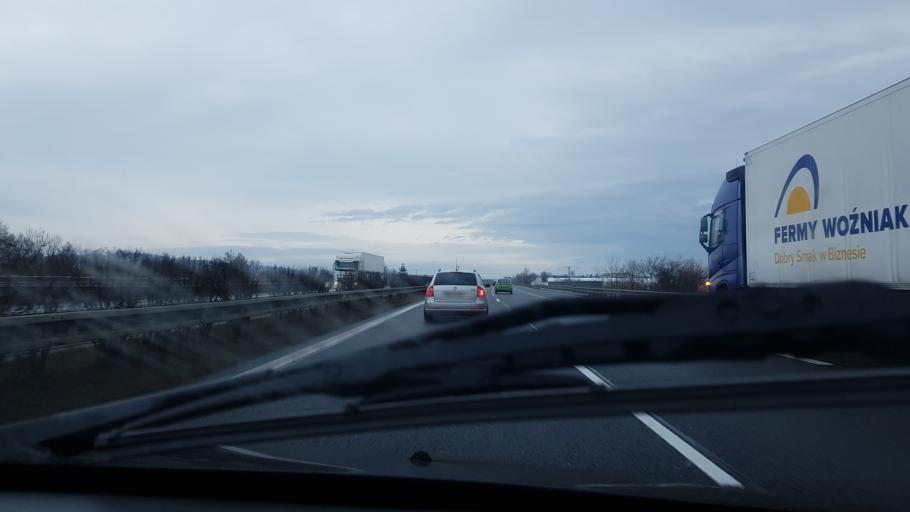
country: CZ
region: Olomoucky
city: Velky Ujezd
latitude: 49.5792
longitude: 17.4649
